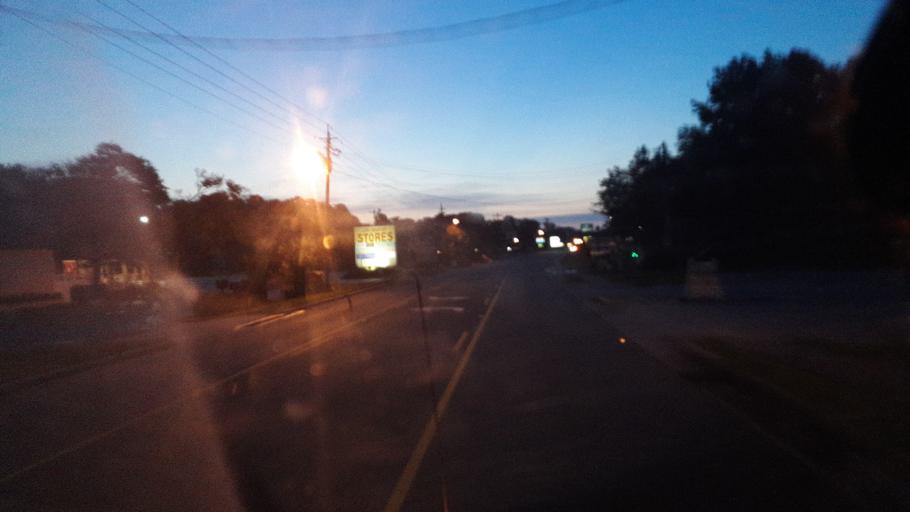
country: US
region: North Carolina
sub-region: Brunswick County
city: Calabash
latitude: 33.8908
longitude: -78.5754
